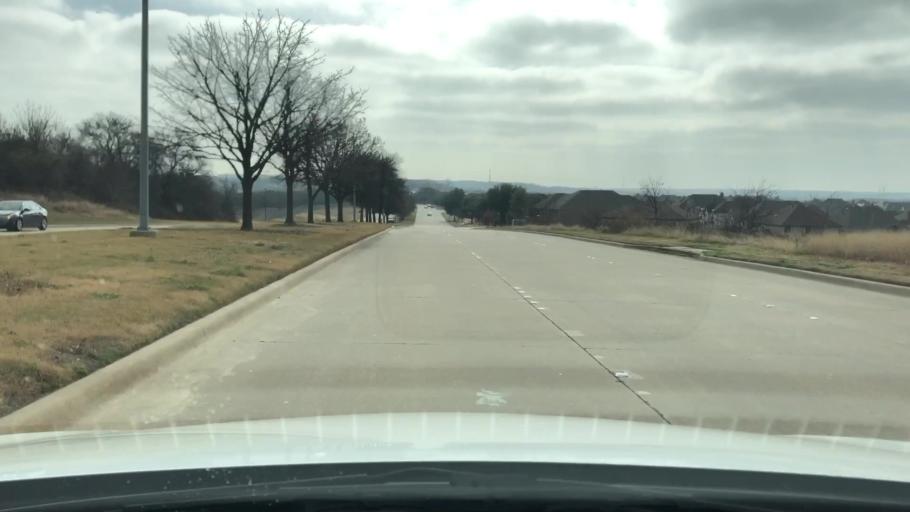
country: US
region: Texas
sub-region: Denton County
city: The Colony
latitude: 33.0773
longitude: -96.8509
